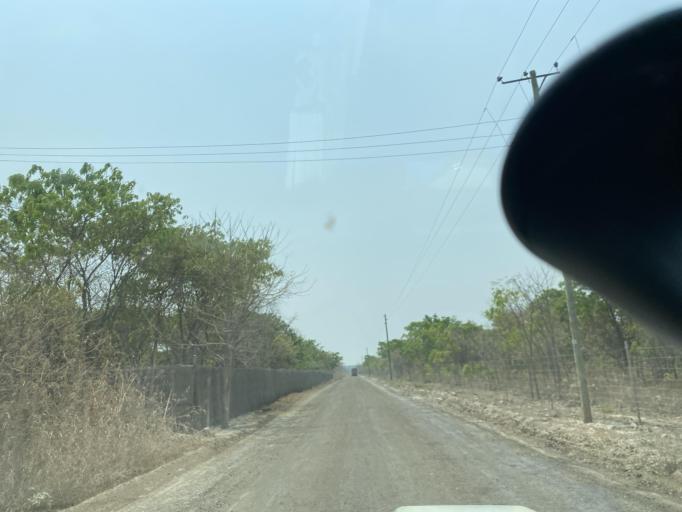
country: ZM
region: Lusaka
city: Lusaka
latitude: -15.5224
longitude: 28.4441
